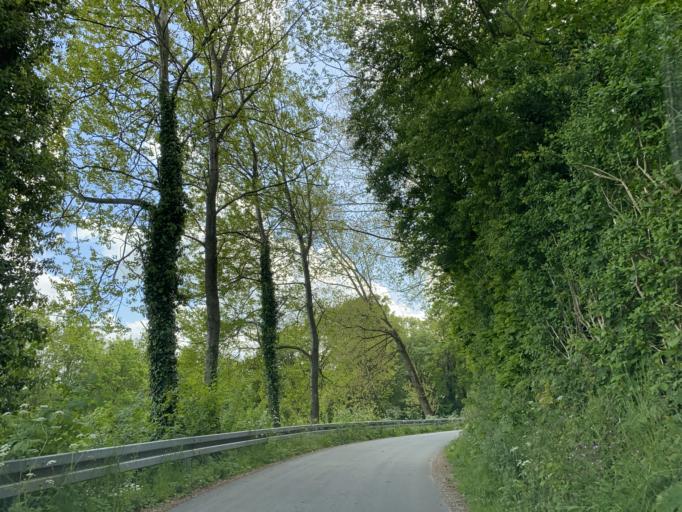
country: DK
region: South Denmark
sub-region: Aabenraa Kommune
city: Lojt Kirkeby
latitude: 55.0096
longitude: 9.4863
